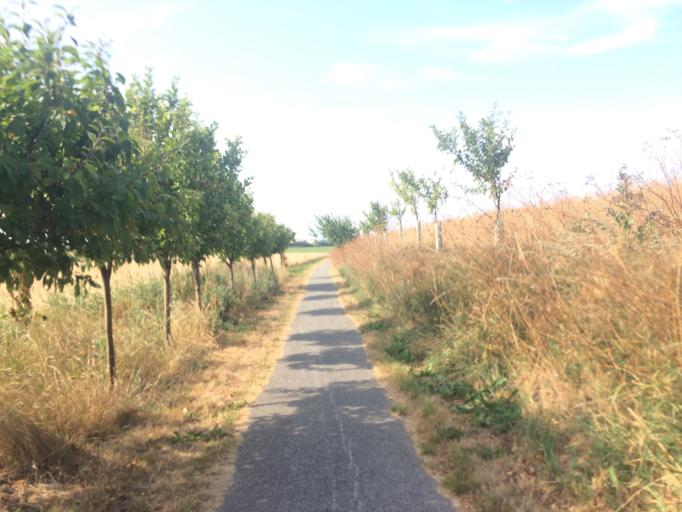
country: DK
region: Central Jutland
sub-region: Holstebro Kommune
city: Vinderup
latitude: 56.6254
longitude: 8.7817
